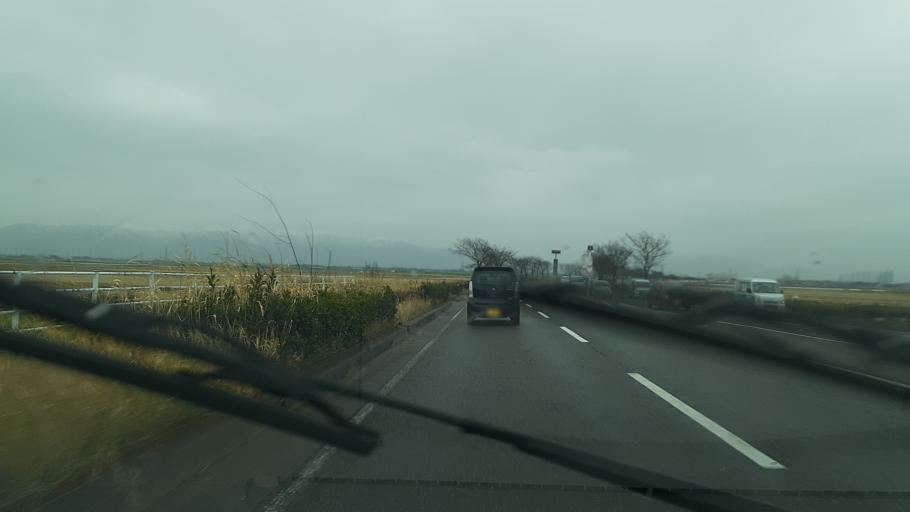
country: JP
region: Niigata
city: Kameda-honcho
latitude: 37.8719
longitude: 139.1349
